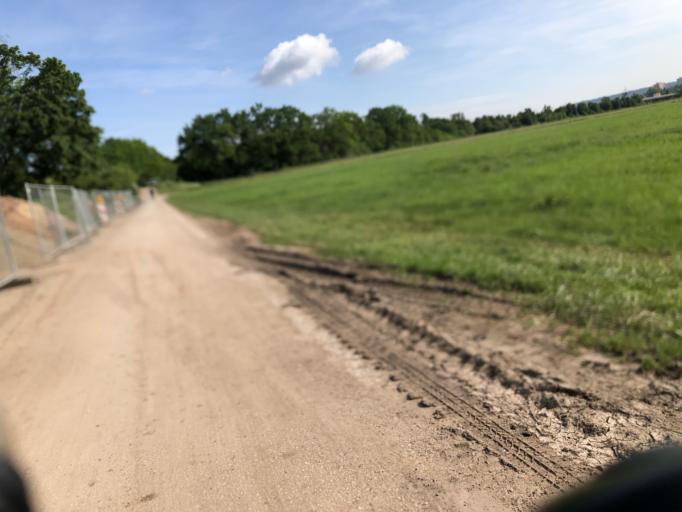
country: DE
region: Bavaria
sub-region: Regierungsbezirk Mittelfranken
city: Erlangen
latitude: 49.5712
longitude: 10.9719
